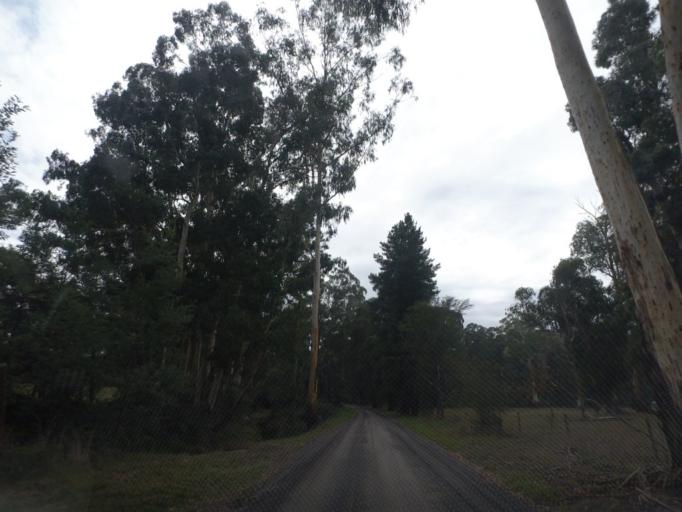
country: AU
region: Victoria
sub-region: Yarra Ranges
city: Healesville
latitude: -37.6410
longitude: 145.5334
